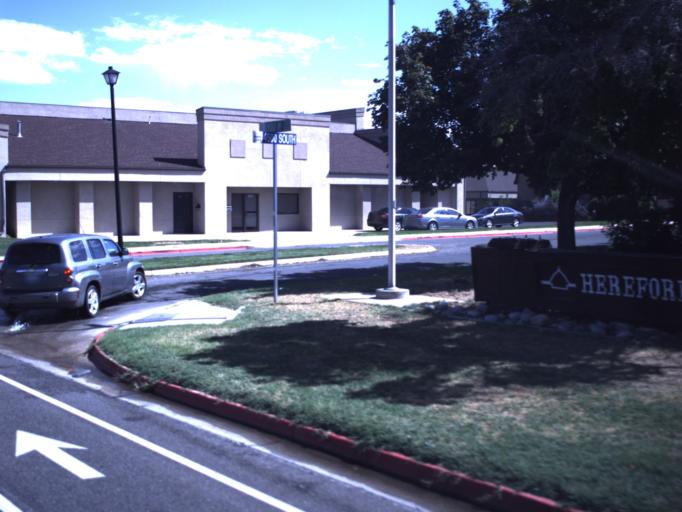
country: US
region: Utah
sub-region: Weber County
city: Roy
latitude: 41.1811
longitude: -112.0259
